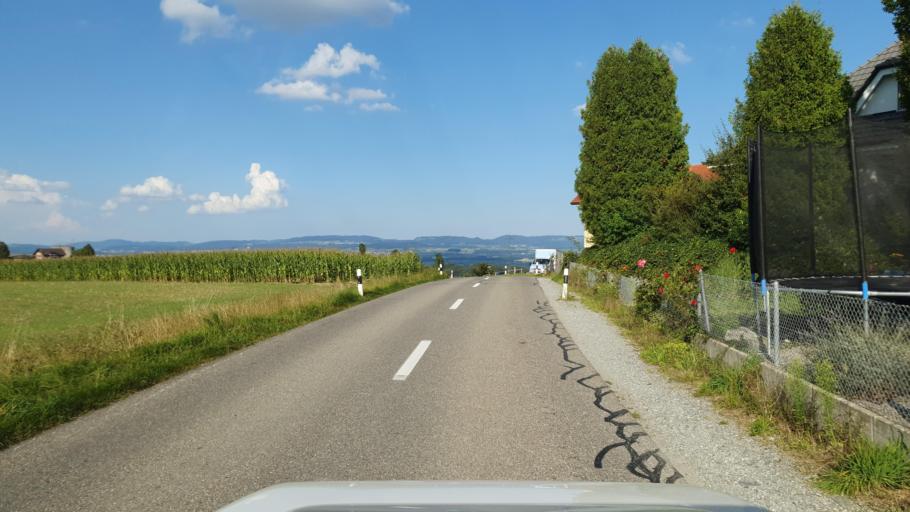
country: CH
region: Aargau
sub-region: Bezirk Muri
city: Auw
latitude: 47.1782
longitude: 8.3573
